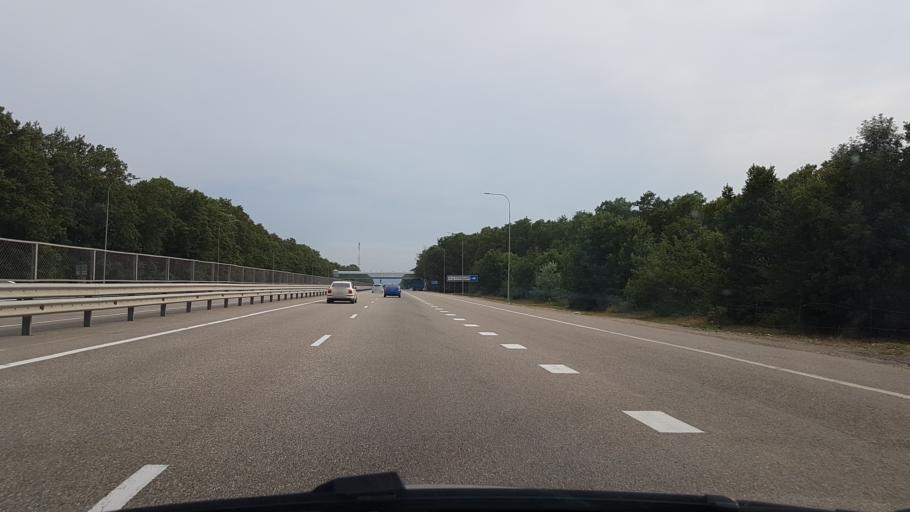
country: RU
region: Krasnodarskiy
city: Saratovskaya
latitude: 44.7146
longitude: 39.2092
